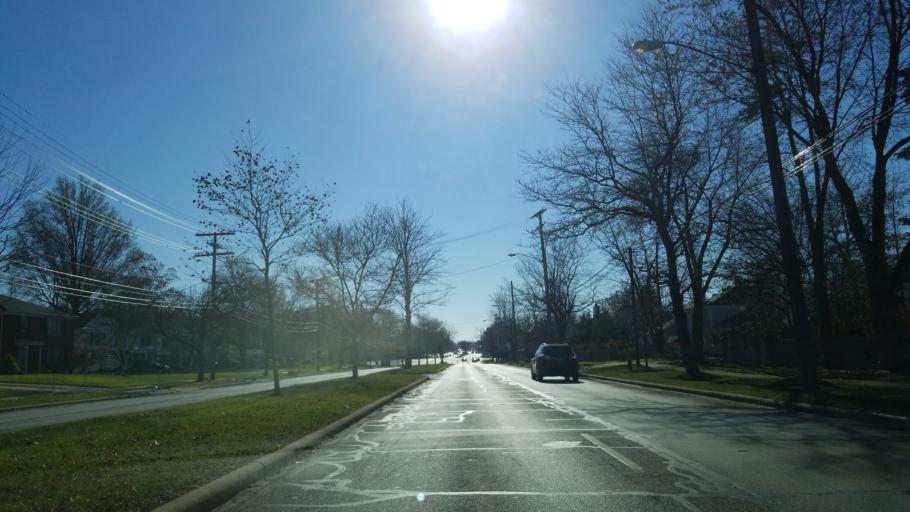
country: US
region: Ohio
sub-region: Cuyahoga County
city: Shaker Heights
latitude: 41.4763
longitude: -81.5363
